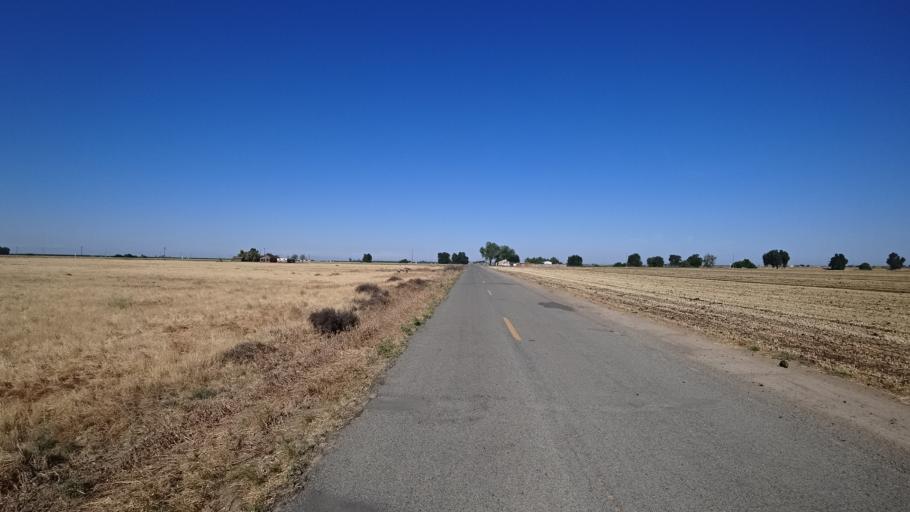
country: US
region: California
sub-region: Kings County
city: Home Garden
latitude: 36.2260
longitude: -119.5625
